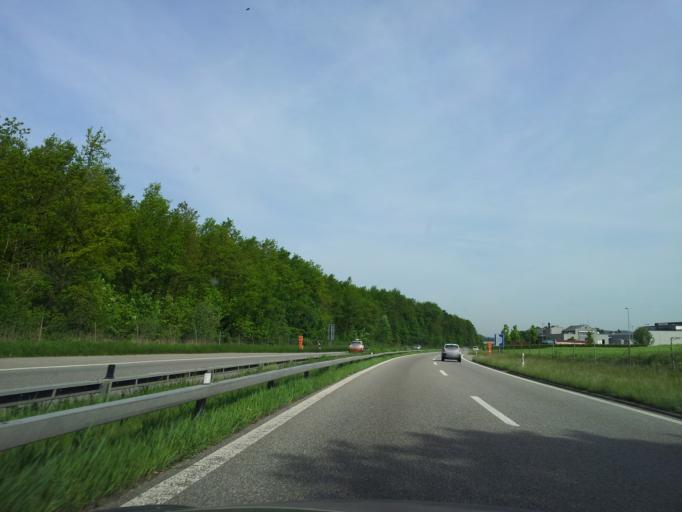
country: CH
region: Zurich
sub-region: Bezirk Buelach
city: Bachenbulach
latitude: 47.4988
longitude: 8.5355
